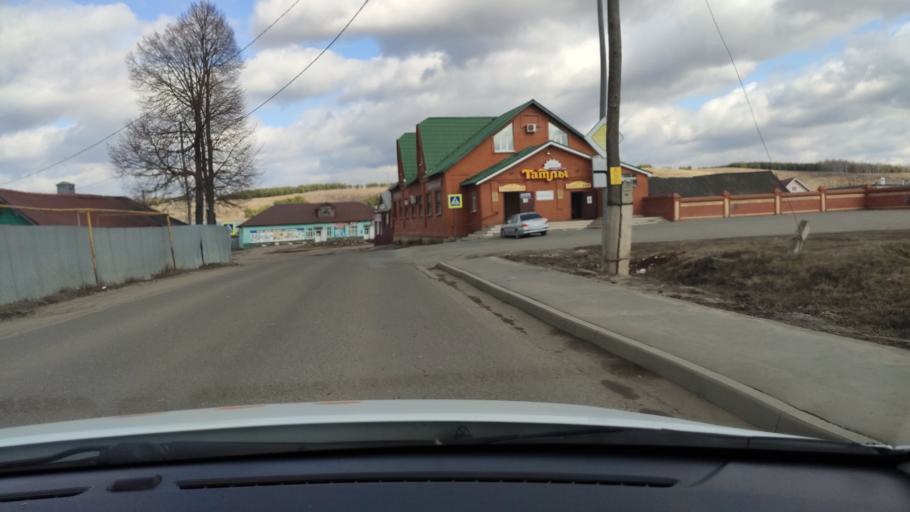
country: RU
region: Tatarstan
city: Vysokaya Gora
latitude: 56.1232
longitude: 49.1973
